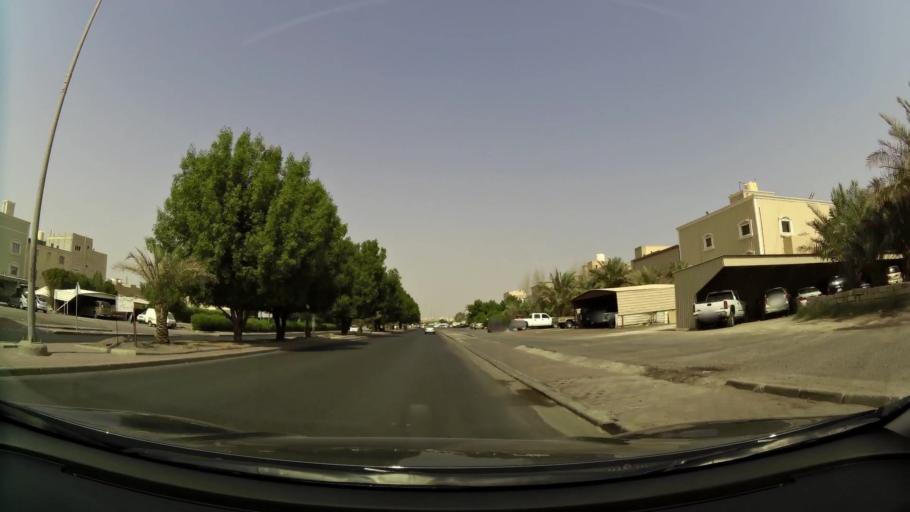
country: KW
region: Muhafazat al Jahra'
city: Al Jahra'
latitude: 29.3255
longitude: 47.6615
